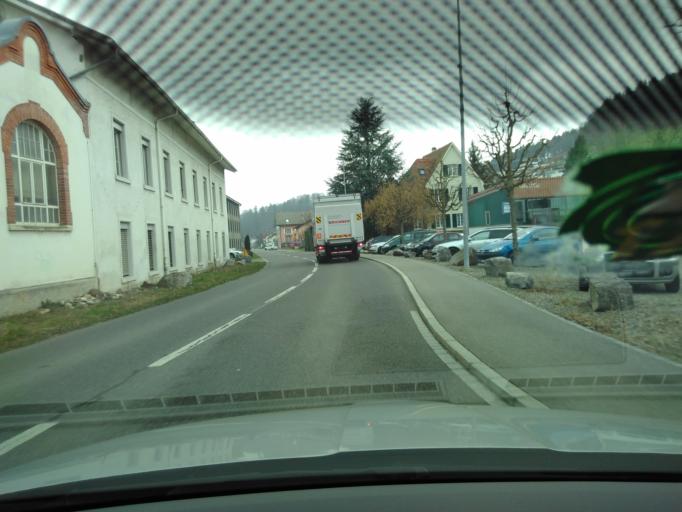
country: CH
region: Aargau
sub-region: Bezirk Aarau
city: Muhen
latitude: 47.3270
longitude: 8.0556
